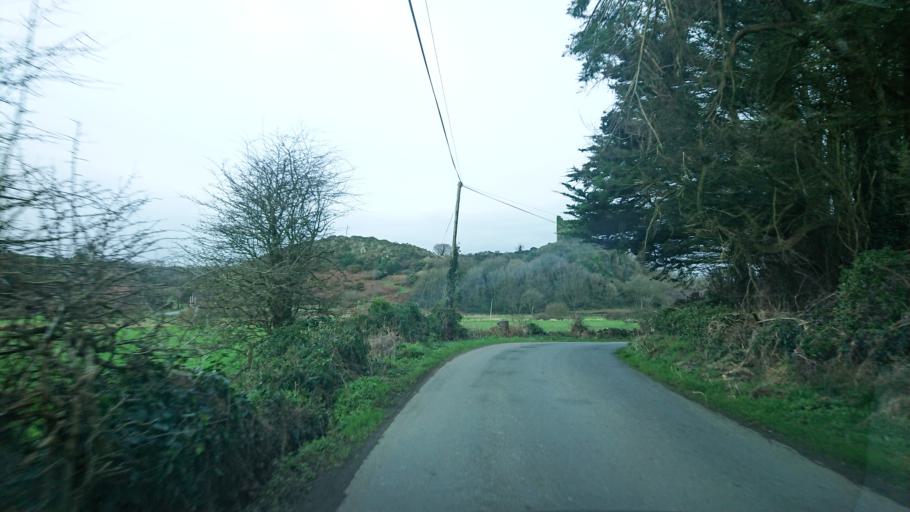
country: IE
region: Munster
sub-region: Waterford
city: Tra Mhor
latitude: 52.1548
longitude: -7.2617
